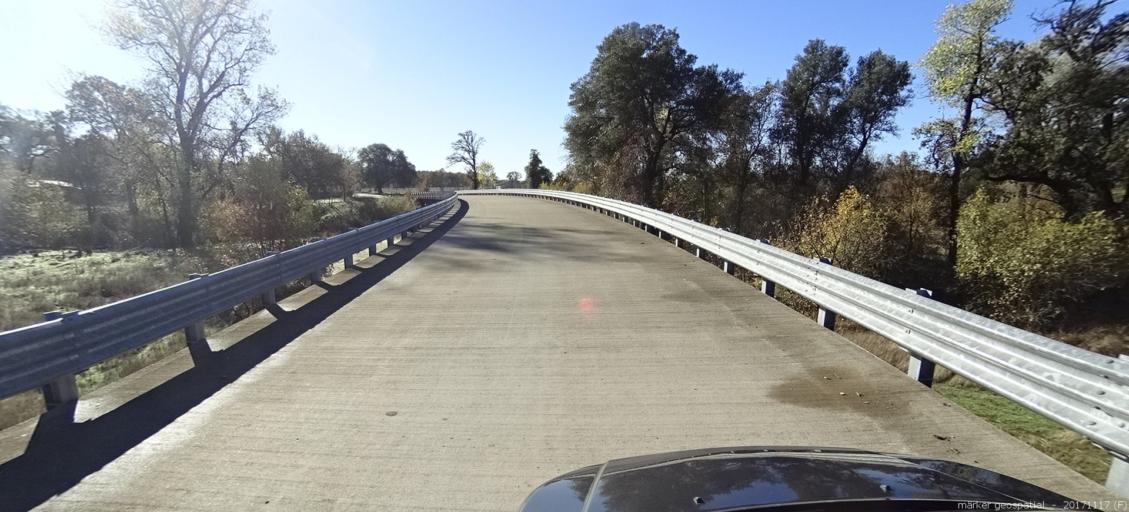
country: US
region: California
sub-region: Shasta County
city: Anderson
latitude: 40.4488
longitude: -122.1973
